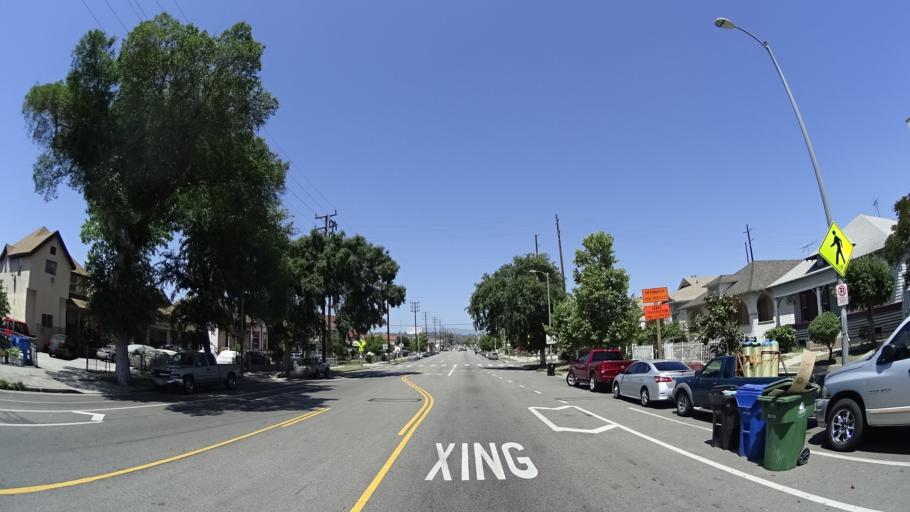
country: US
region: California
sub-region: Los Angeles County
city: Los Angeles
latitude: 34.0712
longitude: -118.2117
